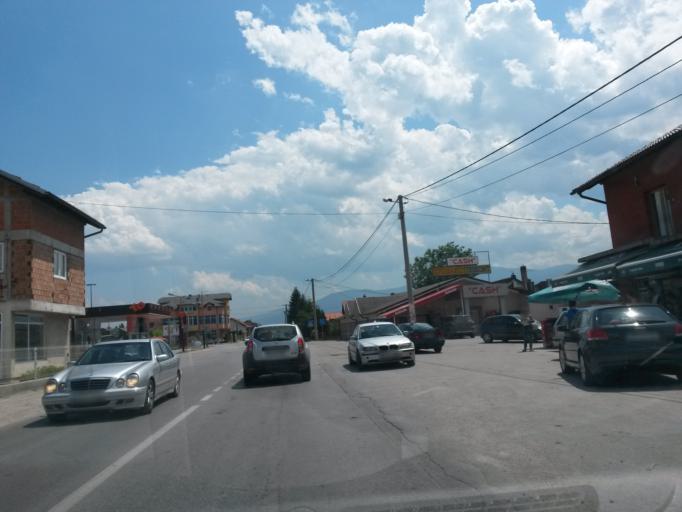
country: BA
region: Federation of Bosnia and Herzegovina
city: Vitez
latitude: 44.1829
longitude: 17.7500
